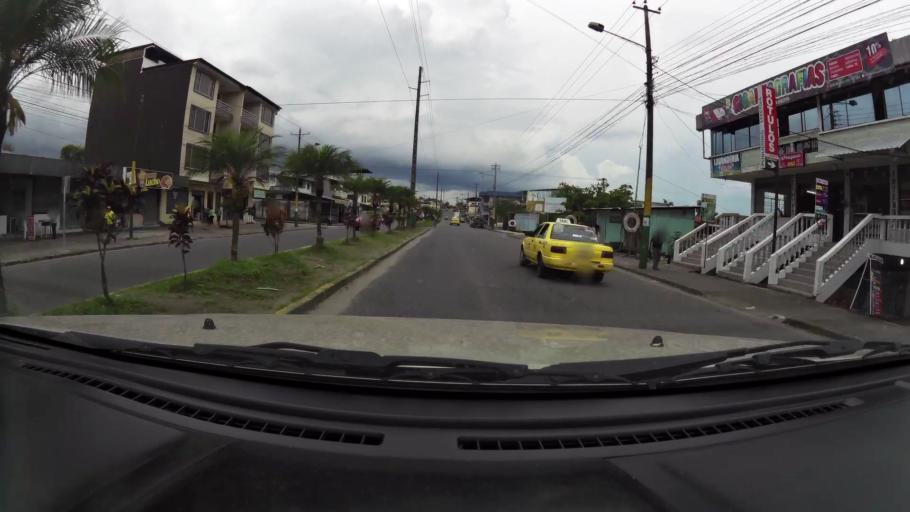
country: EC
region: Pastaza
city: Puyo
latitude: -1.4915
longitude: -78.0103
